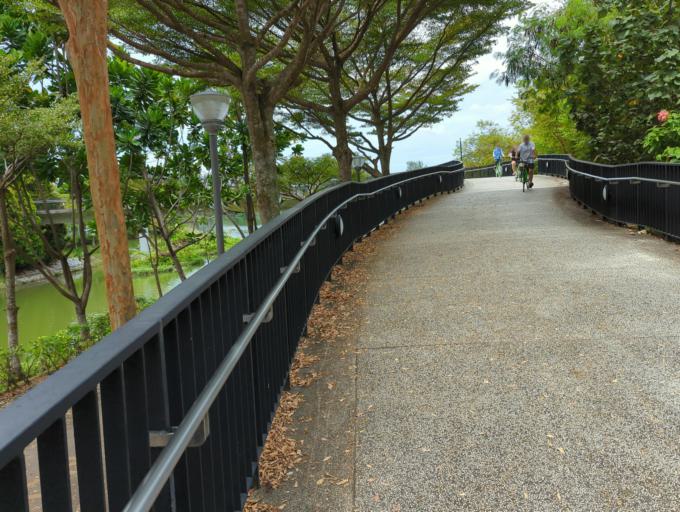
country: MY
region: Johor
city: Kampung Pasir Gudang Baru
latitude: 1.4096
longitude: 103.8963
